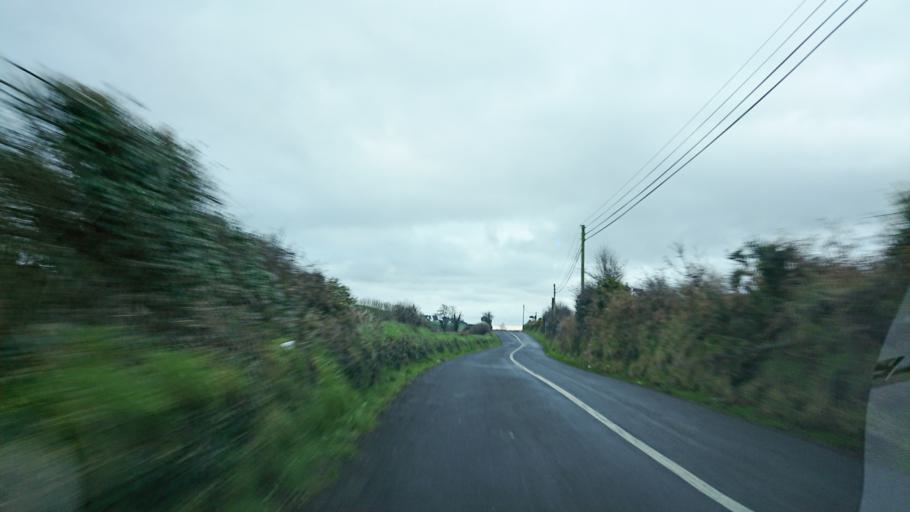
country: IE
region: Munster
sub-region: Waterford
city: Portlaw
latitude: 52.1530
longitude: -7.3814
